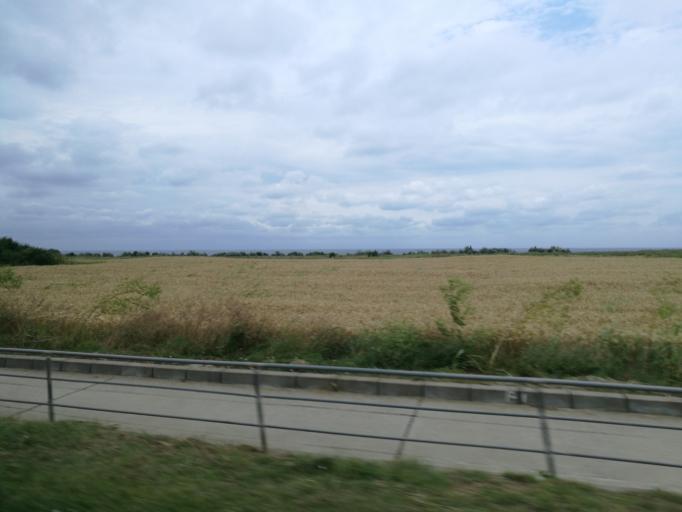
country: RO
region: Constanta
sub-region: Municipiul Mangalia
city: Mangalia
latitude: 43.7680
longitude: 28.5748
